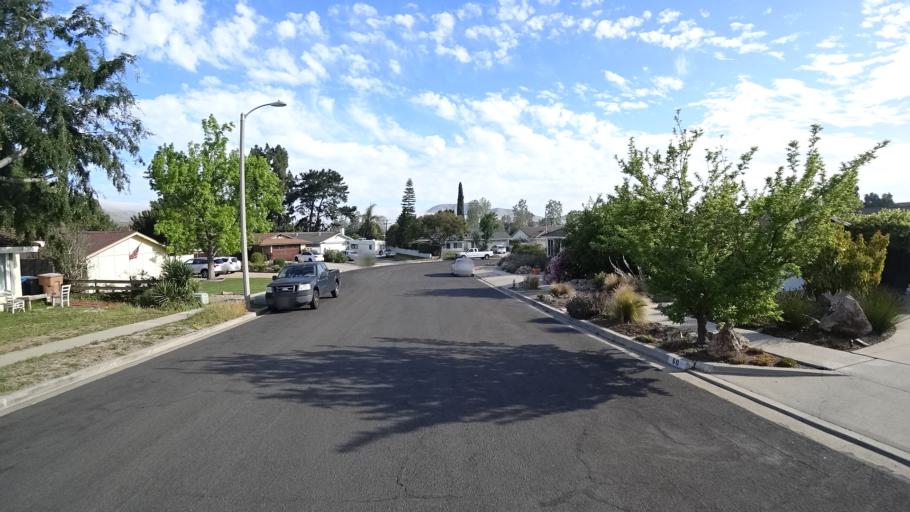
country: US
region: California
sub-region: Ventura County
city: Casa Conejo
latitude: 34.1779
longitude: -118.9514
